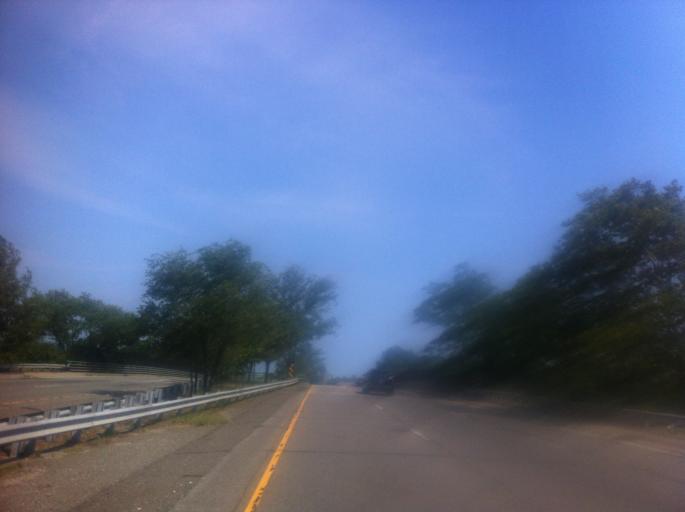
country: US
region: New York
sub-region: Suffolk County
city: North Lindenhurst
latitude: 40.7124
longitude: -73.3725
